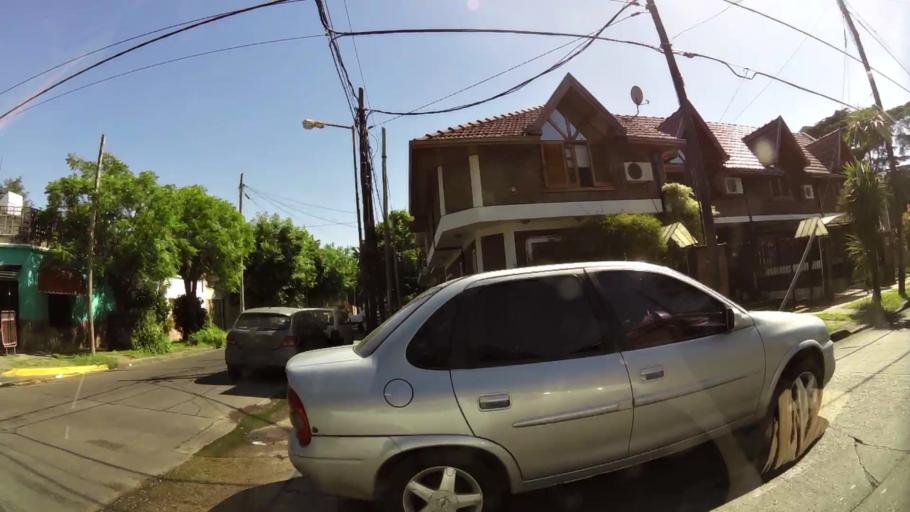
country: AR
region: Buenos Aires
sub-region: Partido de General San Martin
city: General San Martin
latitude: -34.5436
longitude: -58.5716
